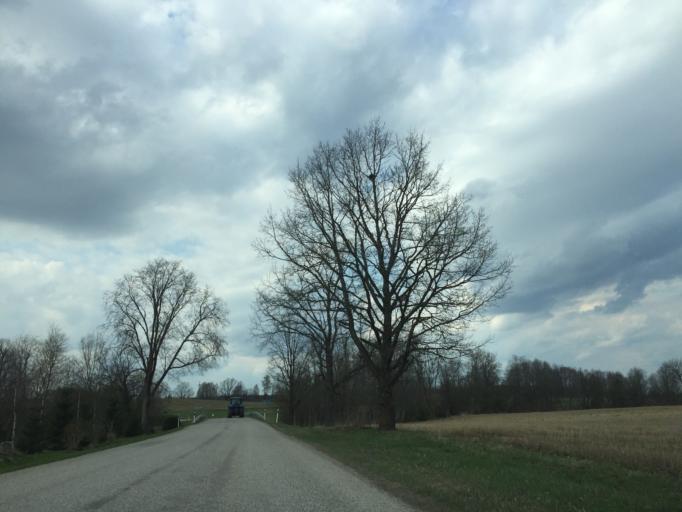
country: RU
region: Pskov
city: Pechory
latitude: 57.7310
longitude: 27.3512
